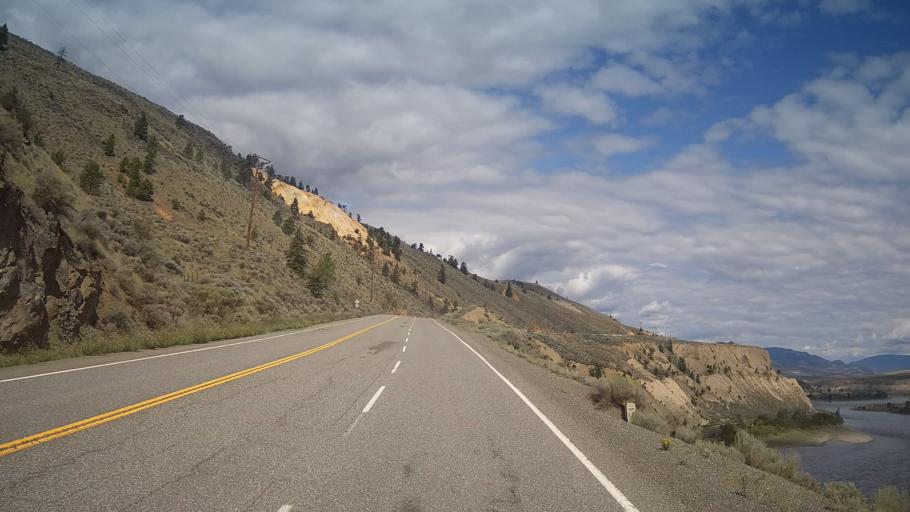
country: CA
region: British Columbia
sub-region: Thompson-Nicola Regional District
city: Ashcroft
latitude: 50.5527
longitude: -121.2975
